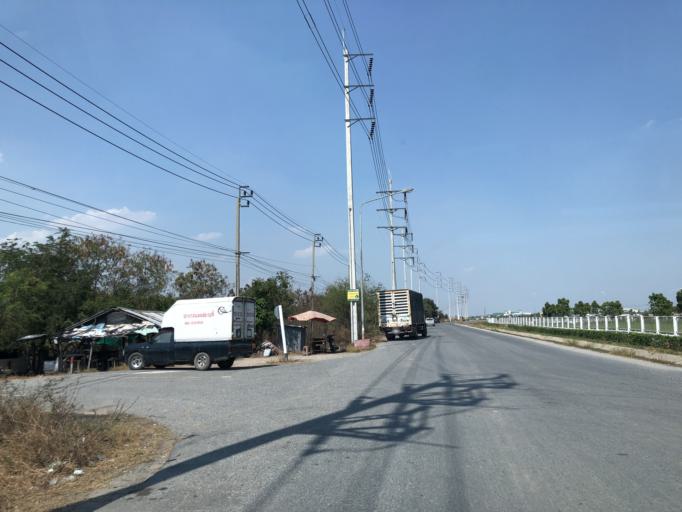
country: TH
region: Samut Prakan
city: Bang Bo District
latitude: 13.5060
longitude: 100.7438
